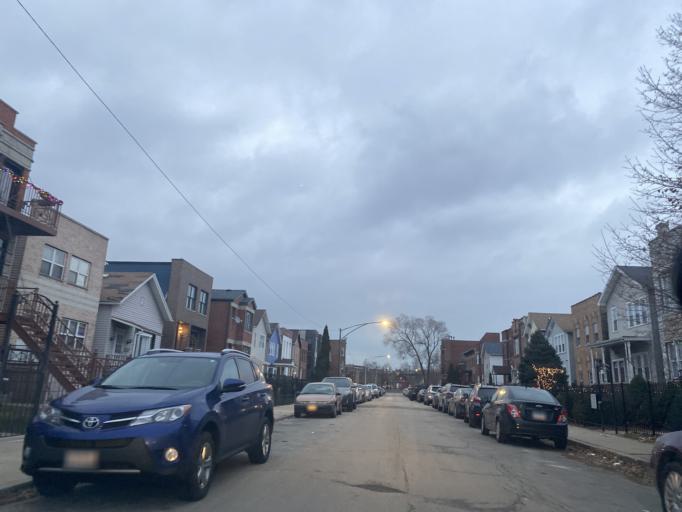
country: US
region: Illinois
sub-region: Cook County
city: Chicago
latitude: 41.8684
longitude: -87.6883
